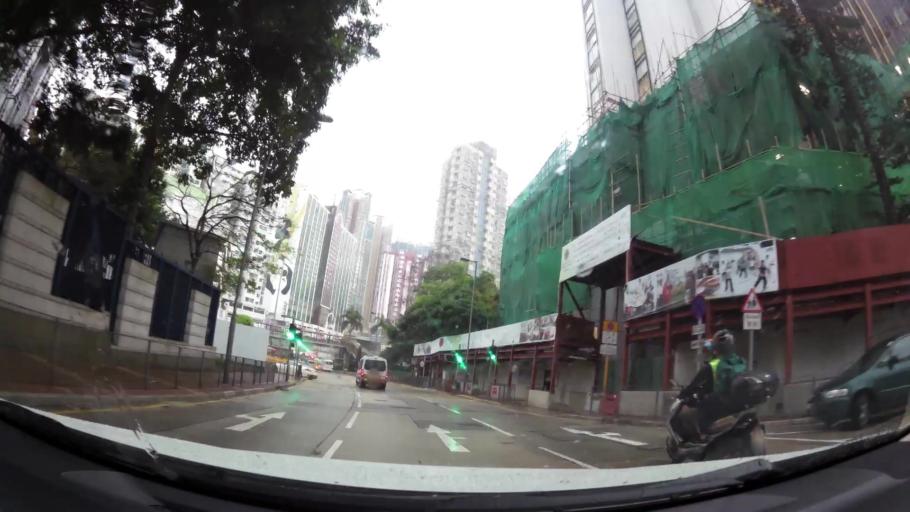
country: HK
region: Tsuen Wan
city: Tsuen Wan
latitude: 22.3713
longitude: 114.1225
